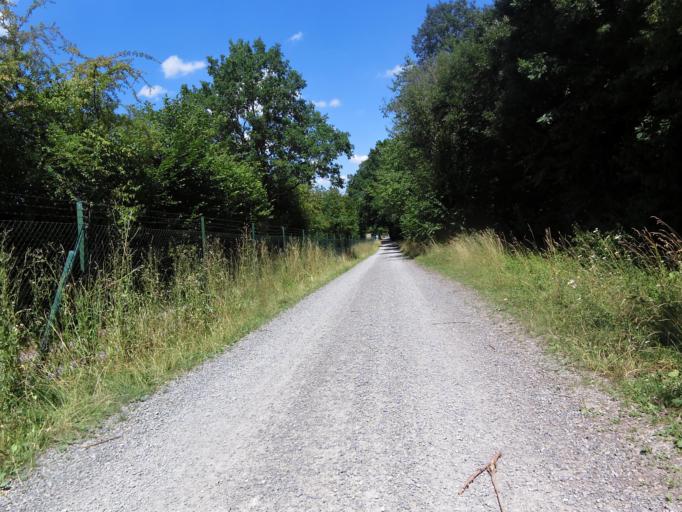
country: DE
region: Bavaria
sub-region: Regierungsbezirk Unterfranken
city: Gadheim
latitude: 49.8275
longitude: 9.9077
